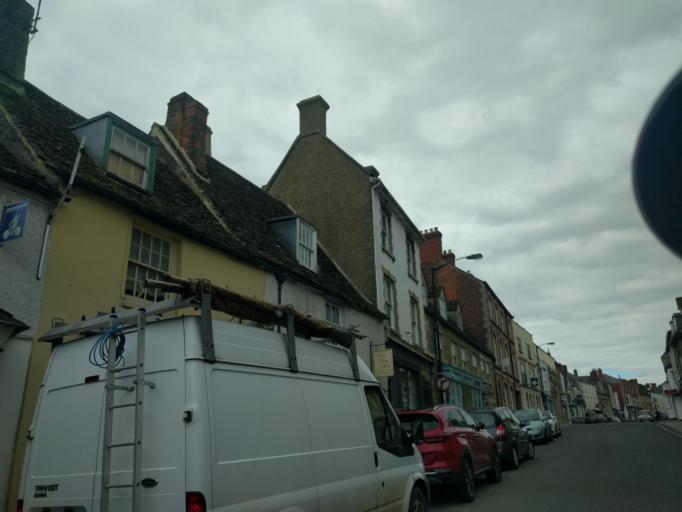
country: GB
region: England
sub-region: Wiltshire
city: Malmesbury
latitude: 51.5821
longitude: -2.0974
